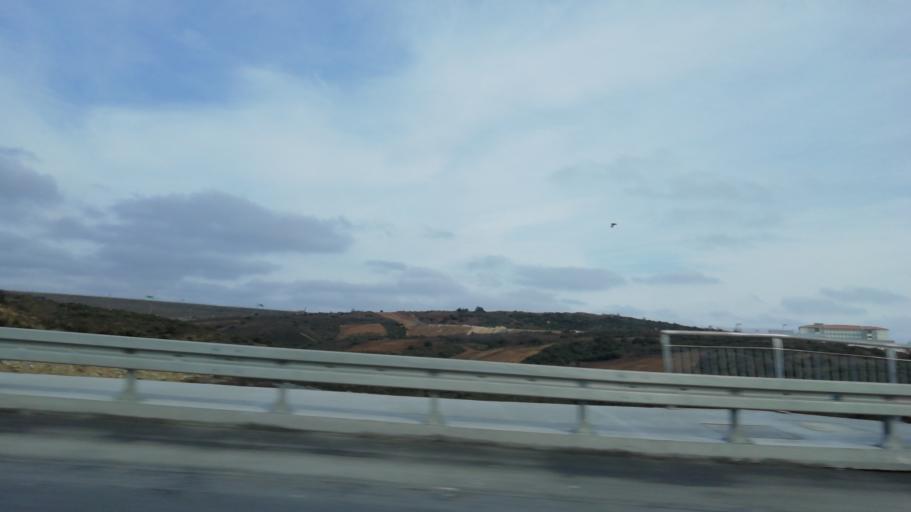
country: TR
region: Istanbul
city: Basaksehir
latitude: 41.1243
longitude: 28.7982
